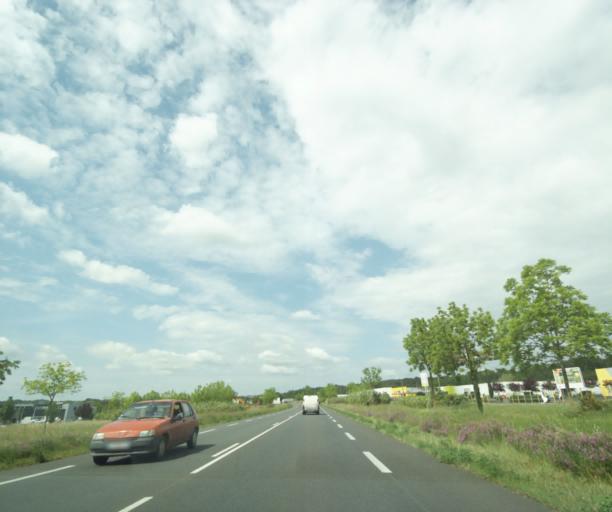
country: FR
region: Pays de la Loire
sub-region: Departement de Maine-et-Loire
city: Distre
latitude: 47.2311
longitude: -0.1133
